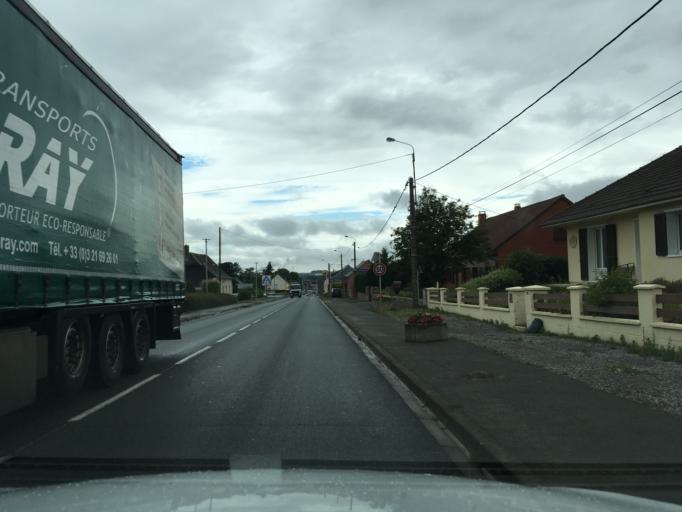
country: FR
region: Picardie
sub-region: Departement de l'Aisne
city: Origny-Sainte-Benoite
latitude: 49.8455
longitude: 3.5064
